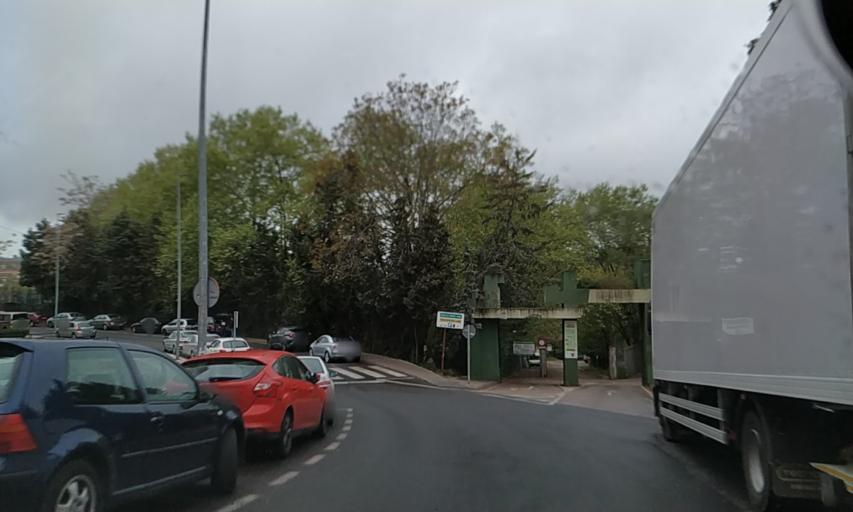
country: ES
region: Extremadura
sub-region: Provincia de Caceres
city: Caceres
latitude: 39.4750
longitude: -6.3799
